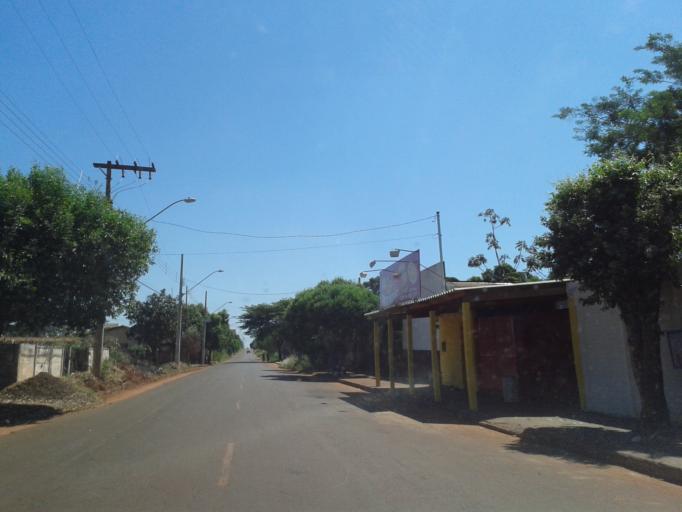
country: BR
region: Minas Gerais
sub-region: Ituiutaba
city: Ituiutaba
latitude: -19.0004
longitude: -49.4544
